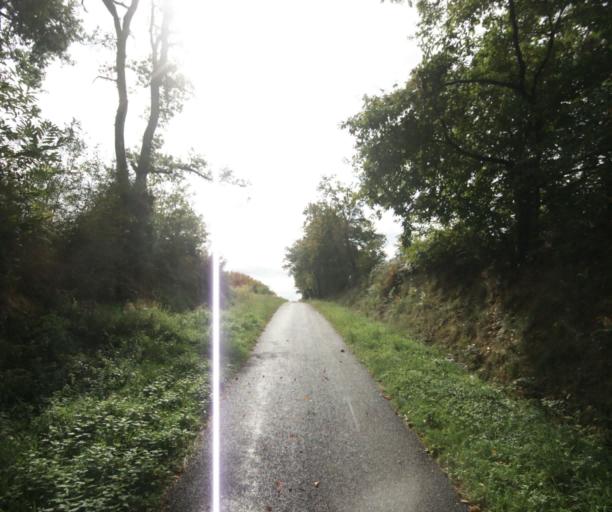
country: FR
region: Midi-Pyrenees
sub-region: Departement du Gers
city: Cazaubon
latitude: 43.9166
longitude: -0.1617
